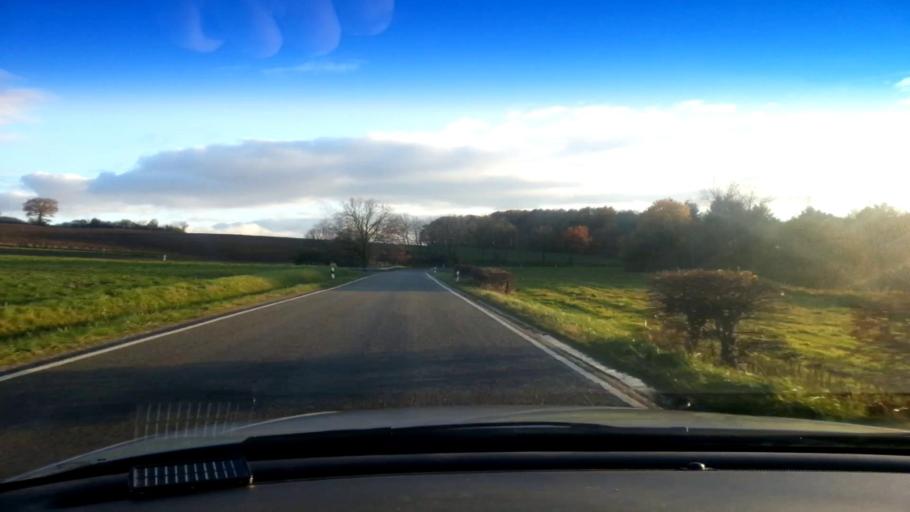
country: DE
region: Bavaria
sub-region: Upper Franconia
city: Hirschaid
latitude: 49.8488
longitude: 11.0211
